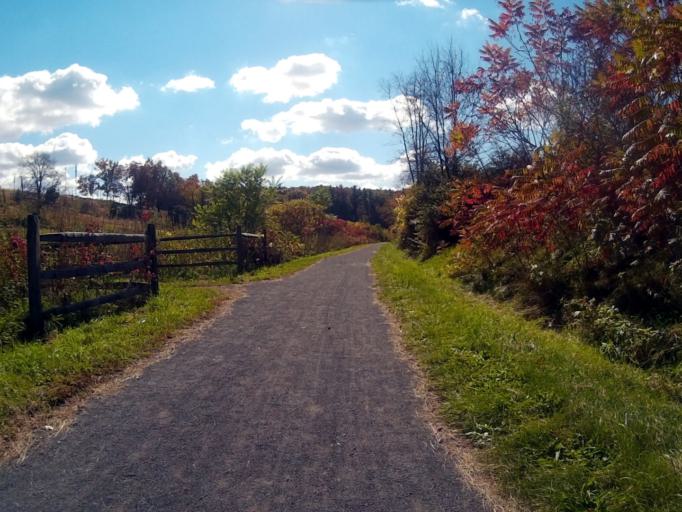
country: US
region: Pennsylvania
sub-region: Centre County
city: State College
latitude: 40.8122
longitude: -77.8752
